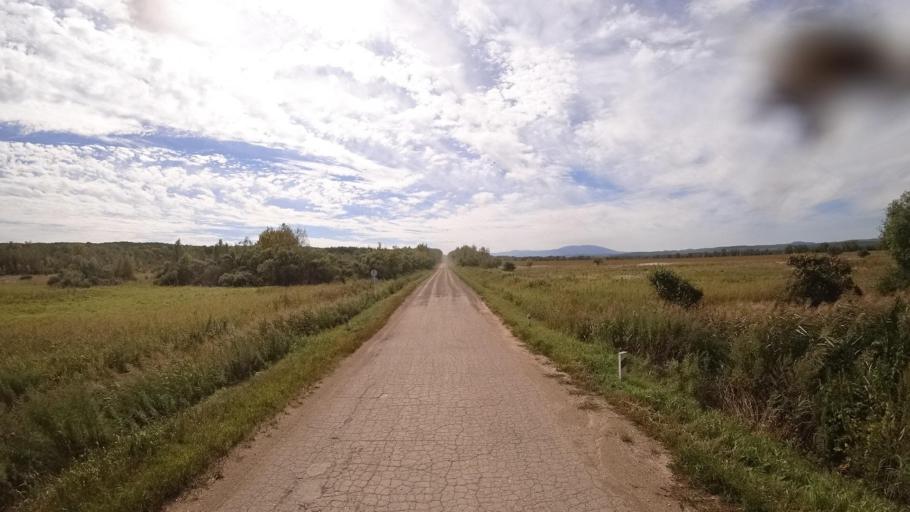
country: RU
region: Primorskiy
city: Yakovlevka
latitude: 44.5608
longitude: 133.5941
